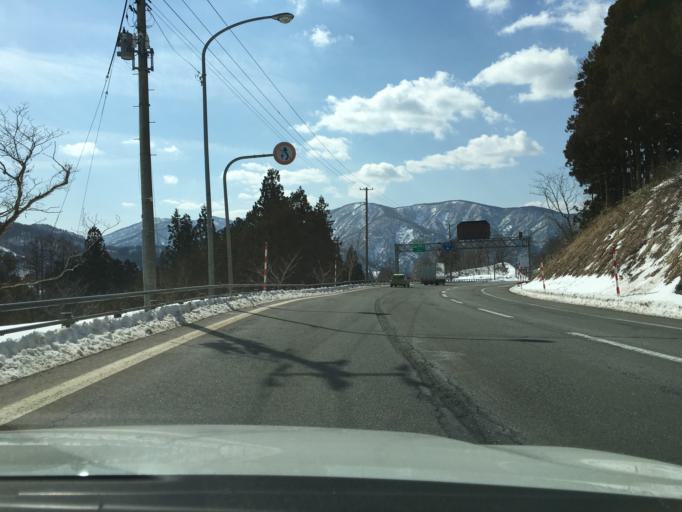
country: JP
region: Yamagata
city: Tsuruoka
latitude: 38.5767
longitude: 139.9301
